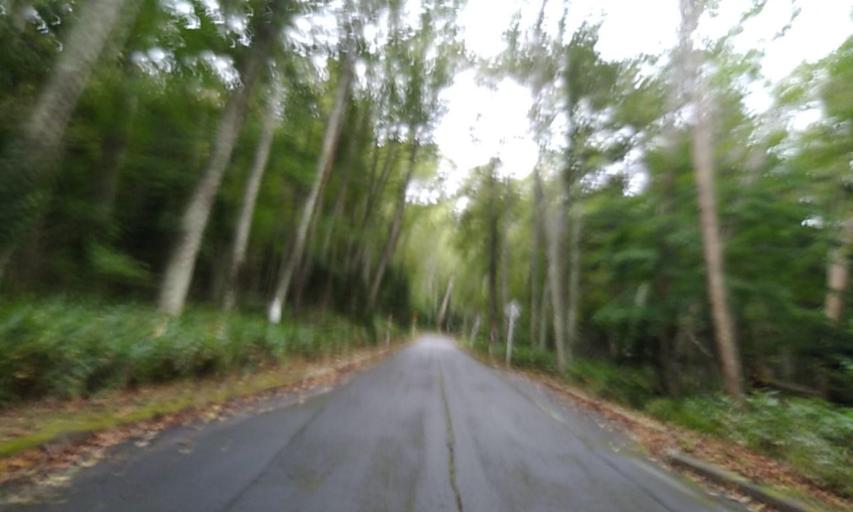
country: JP
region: Hokkaido
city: Bihoro
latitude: 43.5809
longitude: 144.2558
